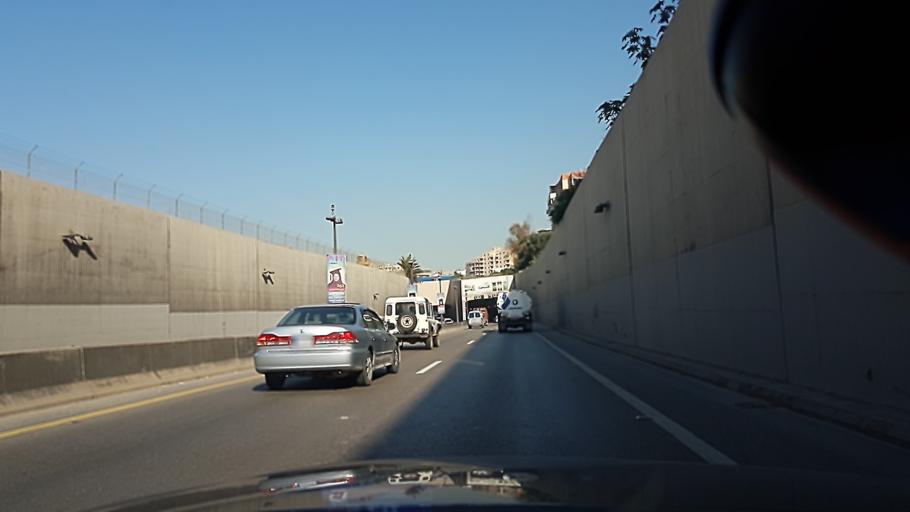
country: LB
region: Mont-Liban
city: Baabda
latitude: 33.8258
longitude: 35.5045
